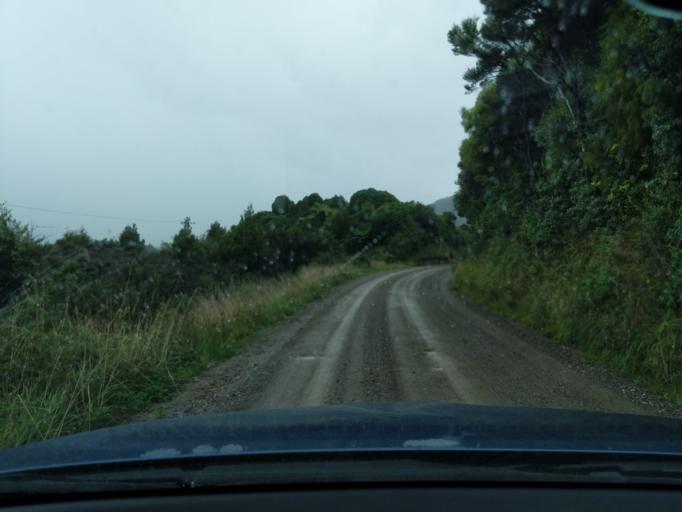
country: NZ
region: Tasman
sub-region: Tasman District
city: Takaka
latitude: -40.6295
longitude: 172.4979
